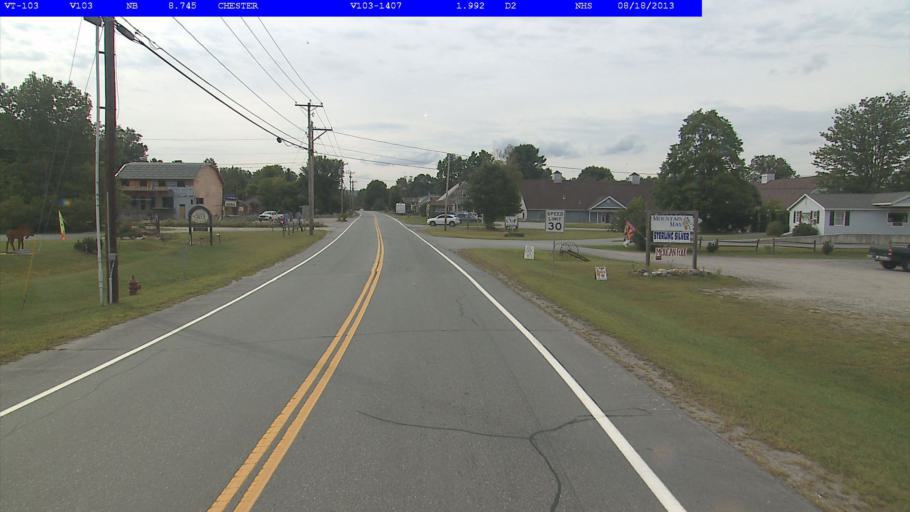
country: US
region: Vermont
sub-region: Windsor County
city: Chester
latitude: 43.2556
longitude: -72.5792
